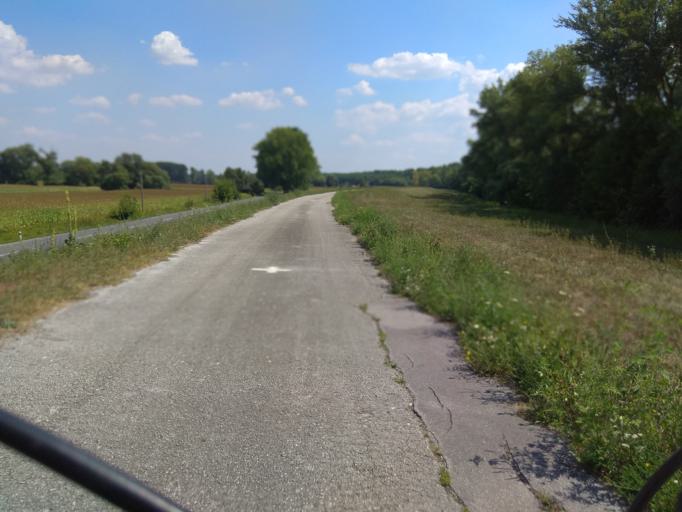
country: SK
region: Trnavsky
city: Gabcikovo
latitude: 47.8159
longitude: 17.6268
